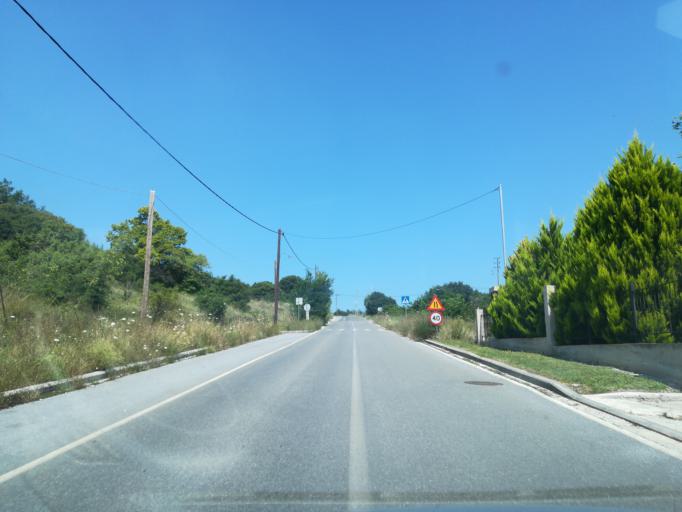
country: GR
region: Central Macedonia
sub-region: Nomos Thessalonikis
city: Asvestochori
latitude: 40.6293
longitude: 23.0354
